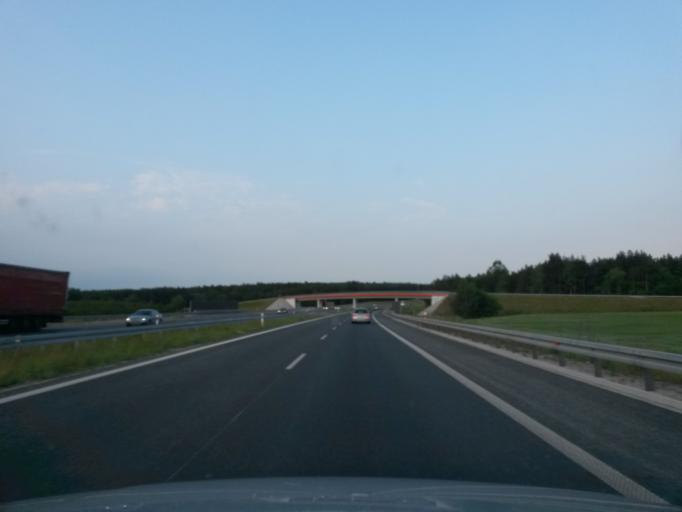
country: PL
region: Greater Poland Voivodeship
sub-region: Powiat kepinski
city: Perzow
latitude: 51.3023
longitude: 17.7761
